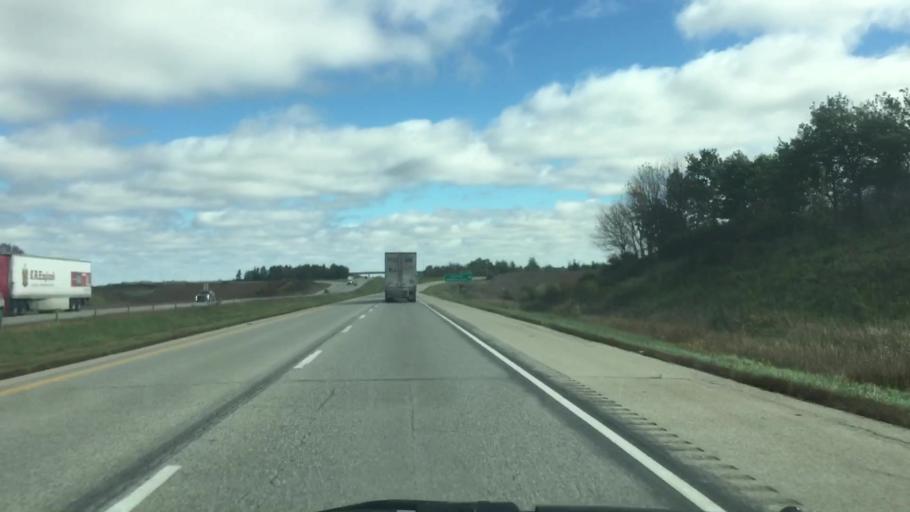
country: US
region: Iowa
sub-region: Poweshiek County
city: Grinnell
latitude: 41.6952
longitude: -92.8069
